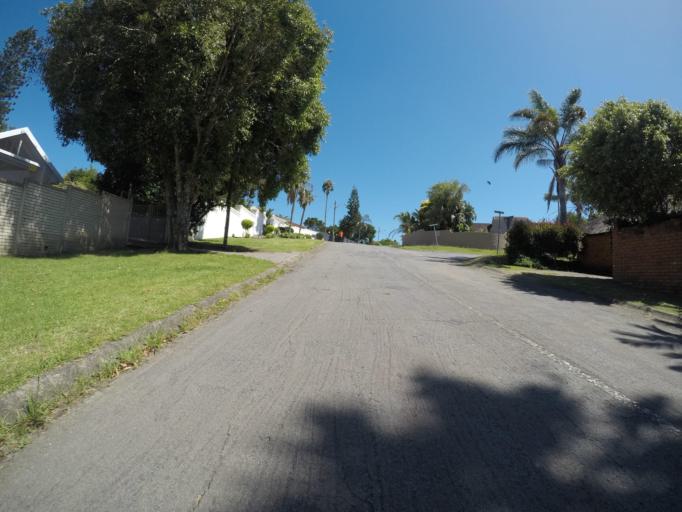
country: ZA
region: Eastern Cape
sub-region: Buffalo City Metropolitan Municipality
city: East London
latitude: -32.9737
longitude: 27.9438
